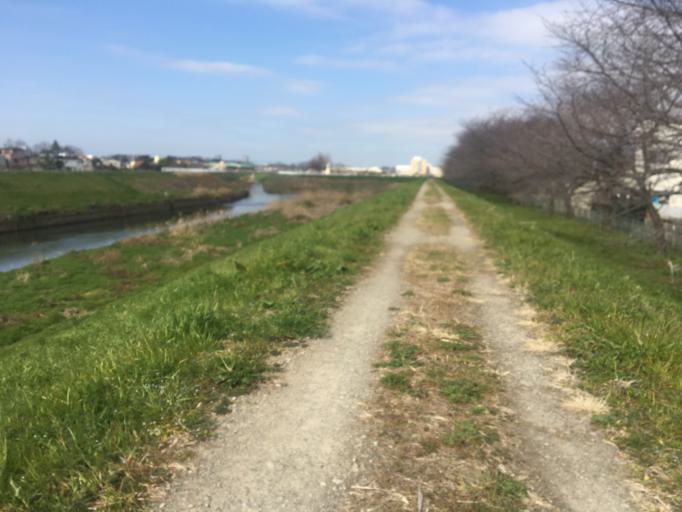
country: JP
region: Saitama
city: Shiki
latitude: 35.8497
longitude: 139.5629
